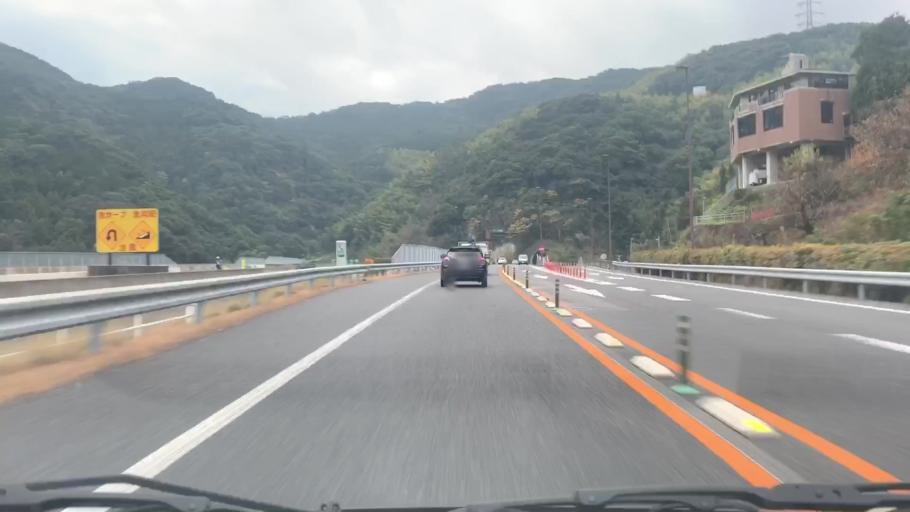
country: JP
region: Nagasaki
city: Nagasaki-shi
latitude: 32.7537
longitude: 129.9282
